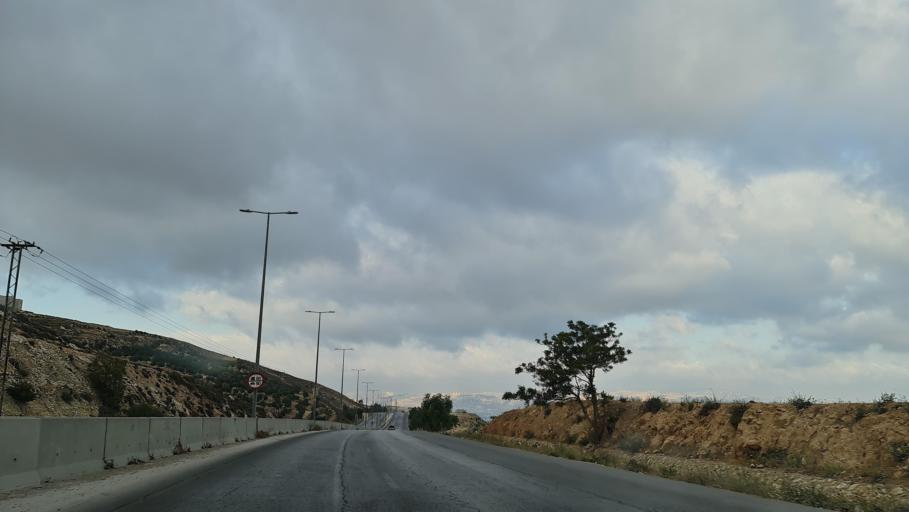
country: JO
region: Amman
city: Al Jubayhah
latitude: 32.0866
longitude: 35.8912
